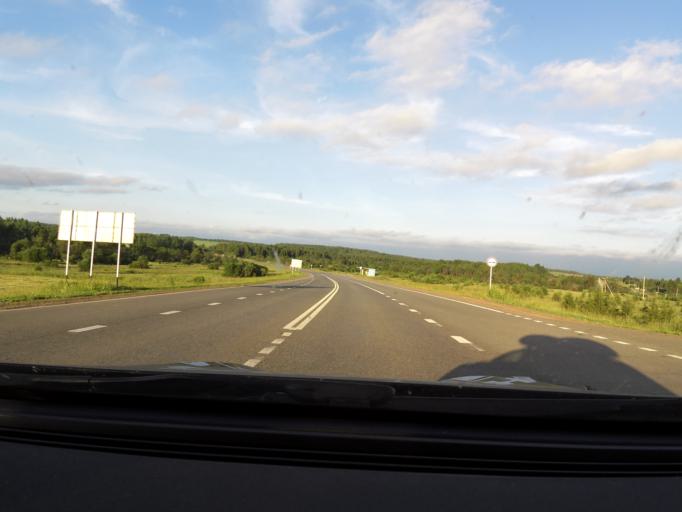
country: RU
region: Perm
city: Siva
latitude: 58.4848
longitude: 54.0736
